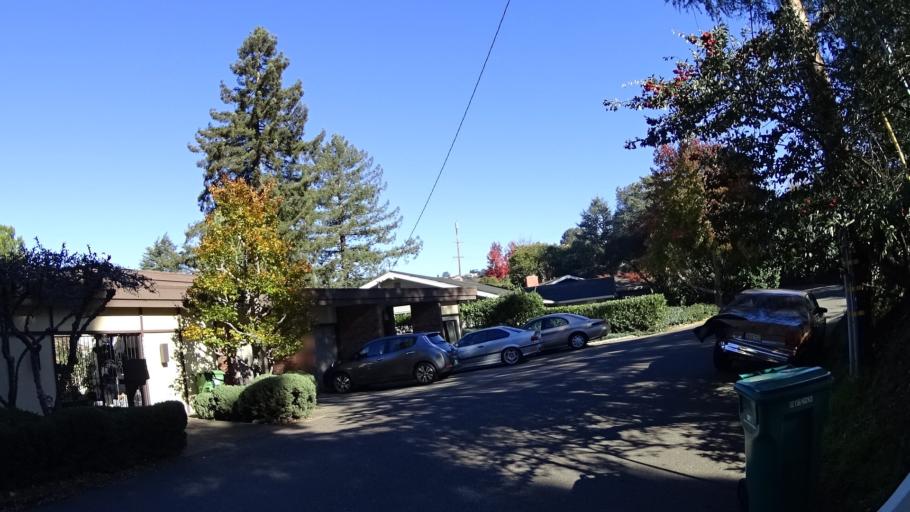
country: US
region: California
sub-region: Alameda County
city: Piedmont
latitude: 37.8289
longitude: -122.2174
